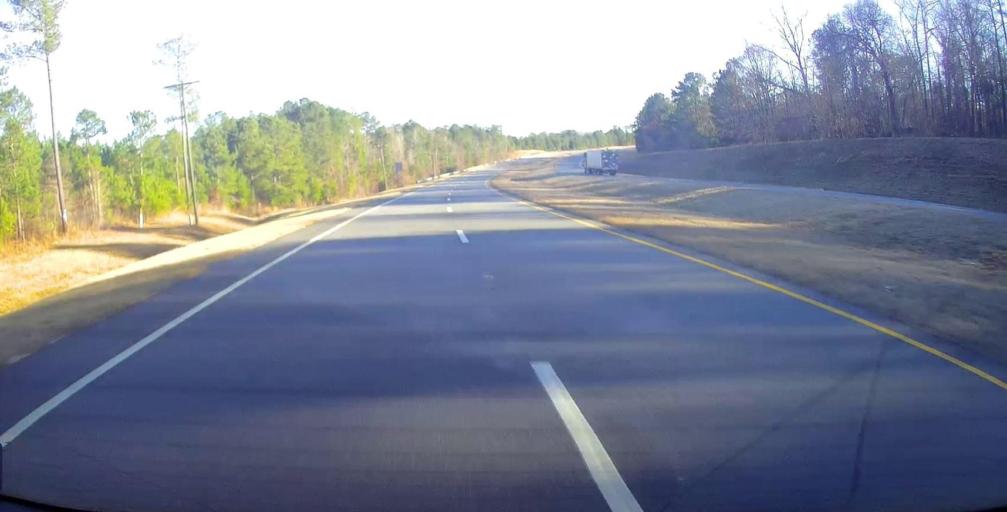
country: US
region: Georgia
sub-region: Upson County
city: Thomaston
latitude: 32.7655
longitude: -84.2449
